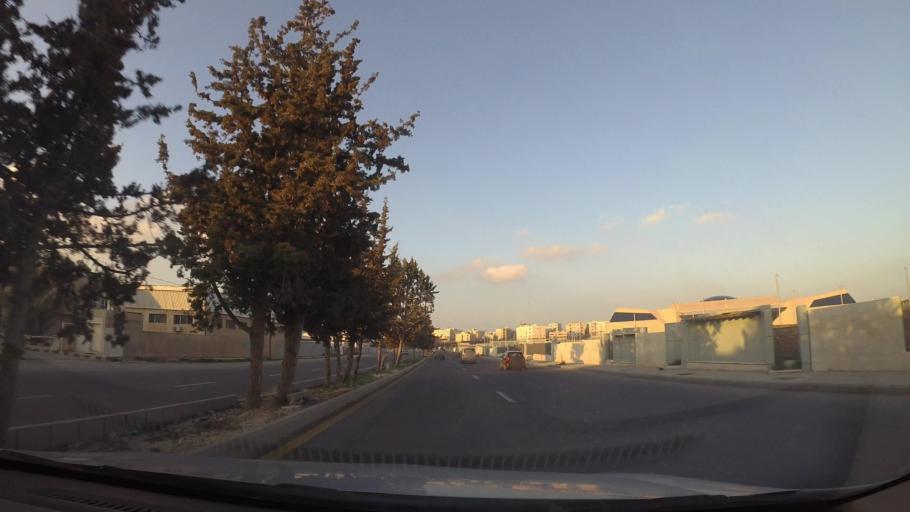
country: JO
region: Amman
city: Al Quwaysimah
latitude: 31.9080
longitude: 35.9220
